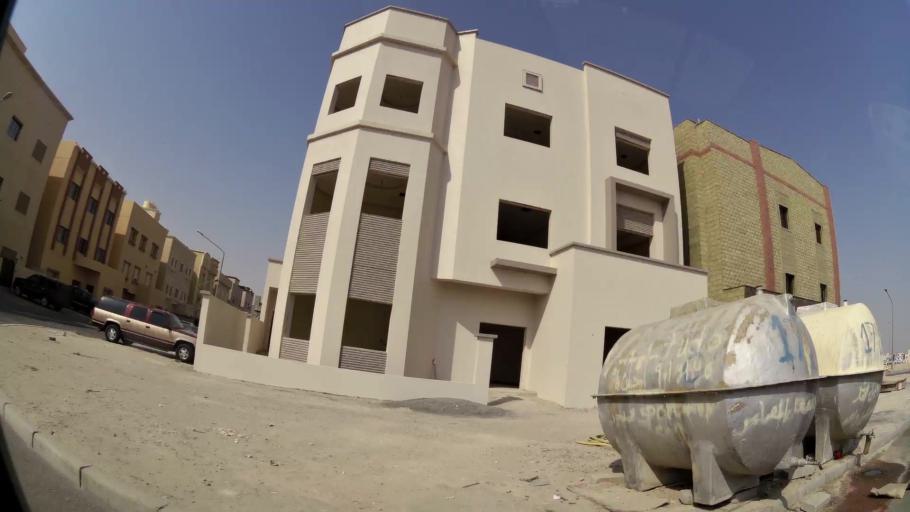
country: KW
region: Muhafazat al Jahra'
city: Al Jahra'
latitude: 29.3400
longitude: 47.7679
